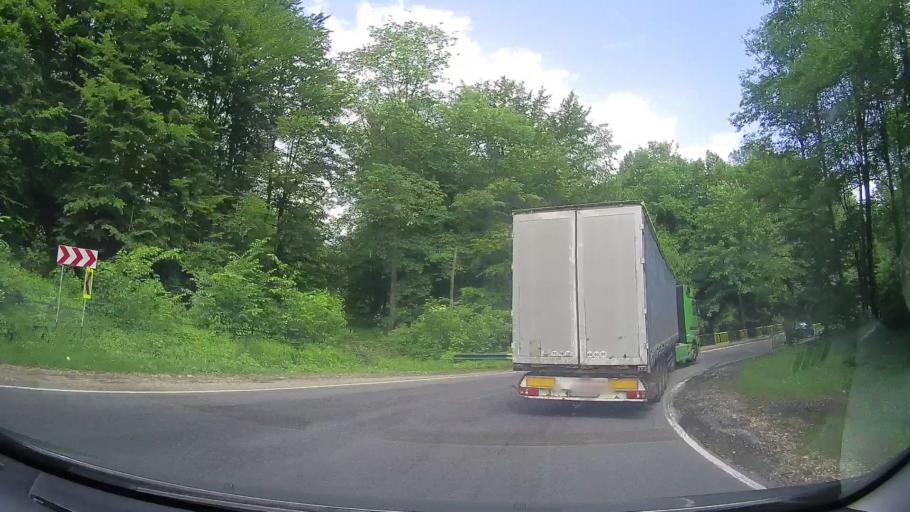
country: RO
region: Prahova
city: Maneciu
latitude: 45.3821
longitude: 25.9283
